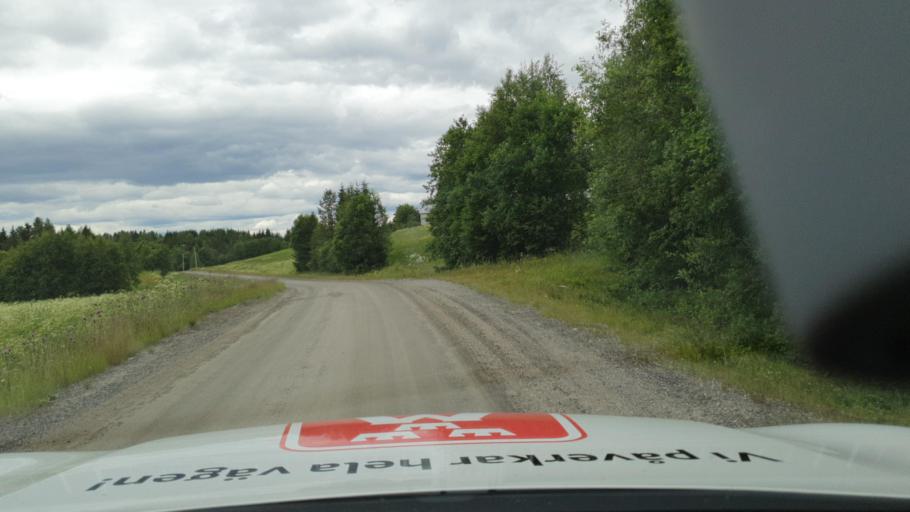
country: SE
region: Vaesterbotten
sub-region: Bjurholms Kommun
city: Bjurholm
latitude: 63.7324
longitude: 19.3019
